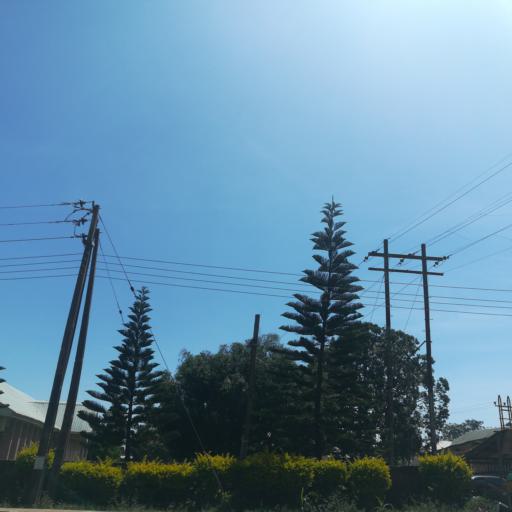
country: NG
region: Plateau
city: Bukuru
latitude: 9.7841
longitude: 8.8617
